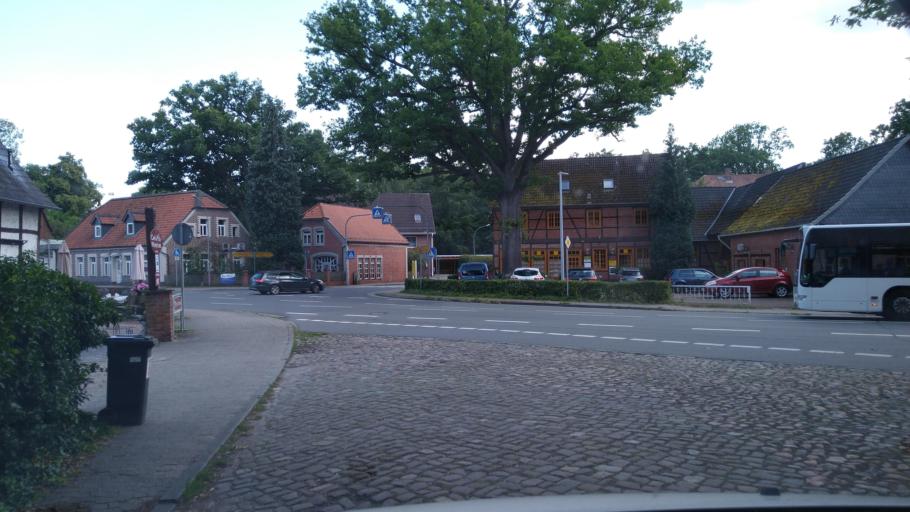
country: DE
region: Lower Saxony
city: Wienhausen
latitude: 52.5800
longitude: 10.1854
